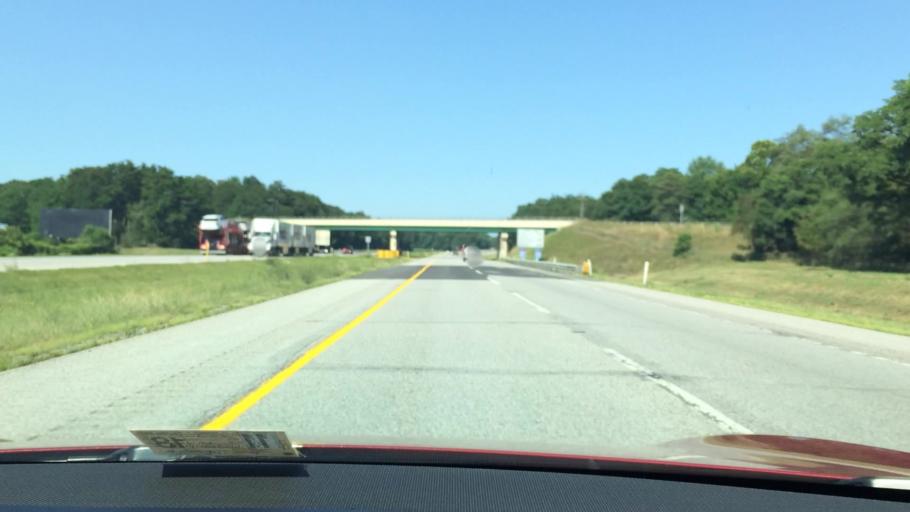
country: US
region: Indiana
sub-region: Elkhart County
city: Bristol
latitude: 41.7349
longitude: -85.7982
